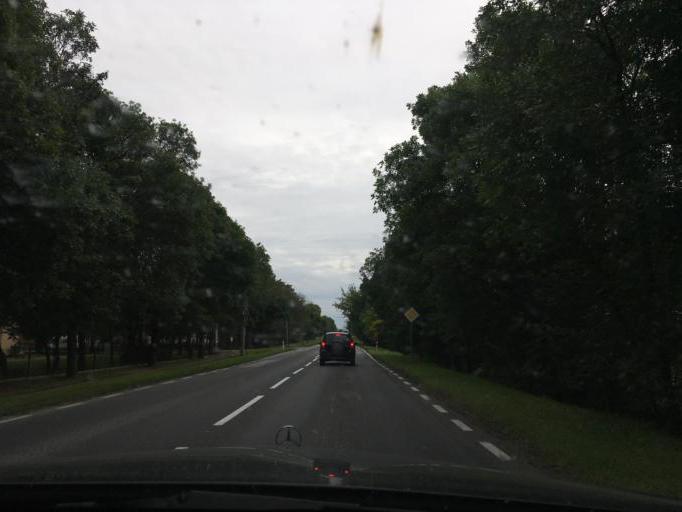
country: PL
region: Masovian Voivodeship
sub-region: Powiat ostrowski
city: Ostrow Mazowiecka
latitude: 52.8400
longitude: 21.8705
